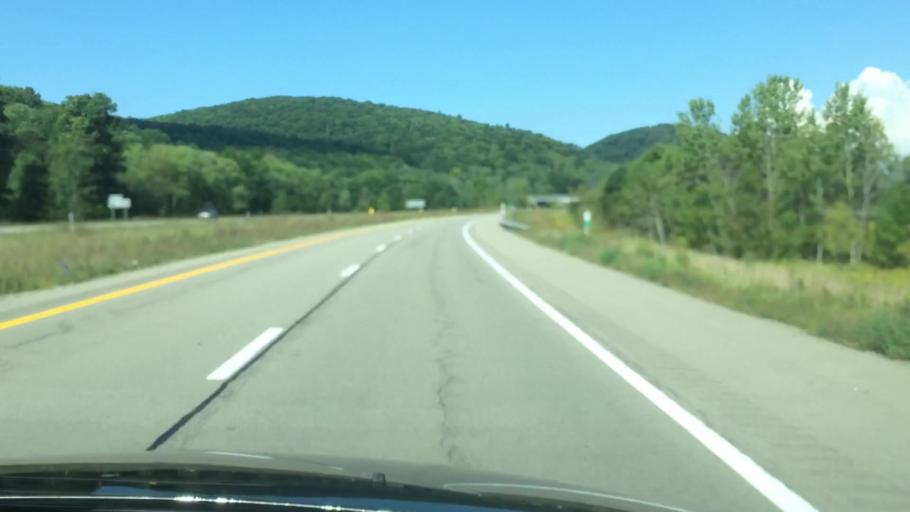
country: US
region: New York
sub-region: Cattaraugus County
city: Randolph
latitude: 42.1047
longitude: -78.9114
